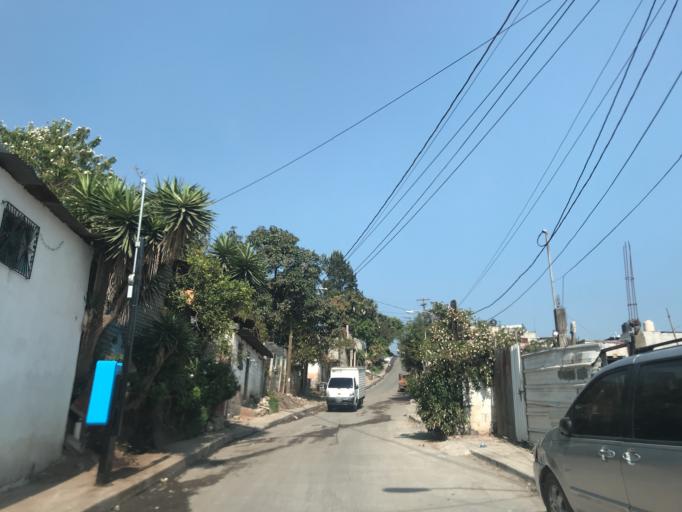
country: GT
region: Guatemala
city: Villa Nueva
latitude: 14.5021
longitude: -90.5882
